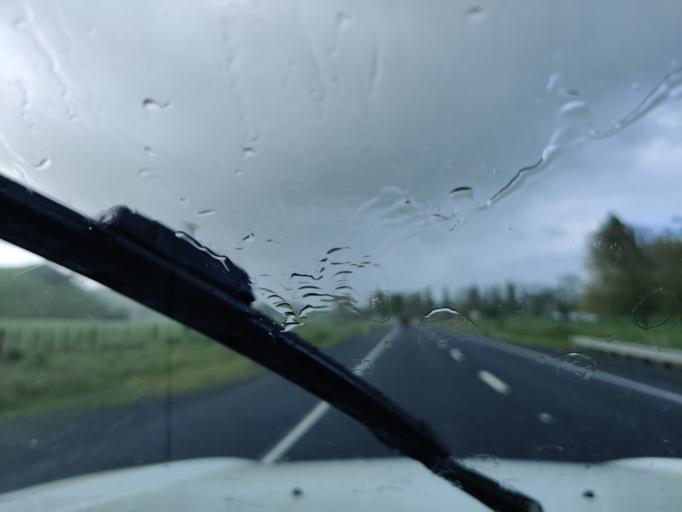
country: NZ
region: Waikato
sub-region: Matamata-Piako District
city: Matamata
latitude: -37.9736
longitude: 175.6943
